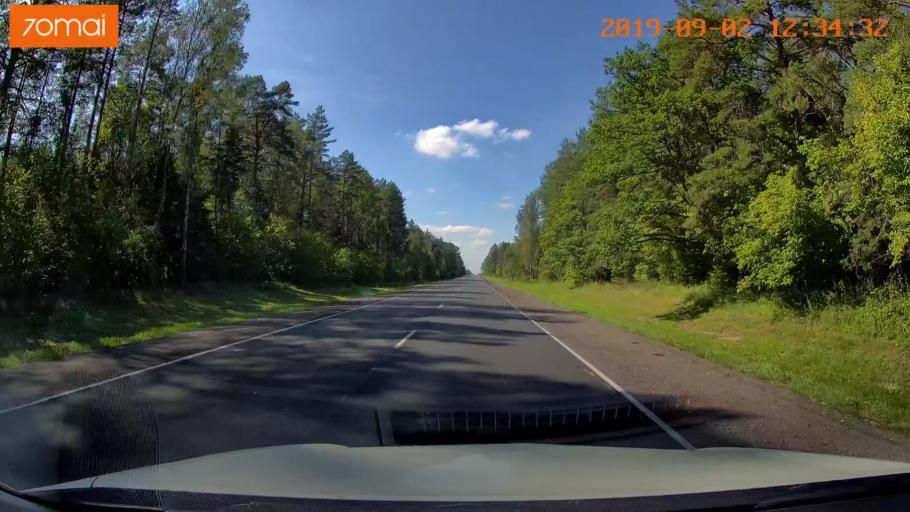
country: RU
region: Smolensk
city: Shumyachi
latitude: 53.8095
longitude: 32.4018
